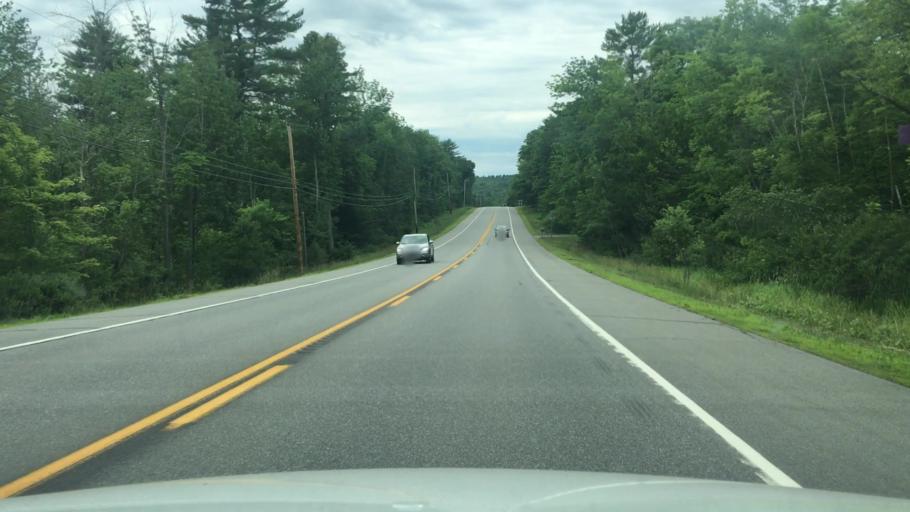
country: US
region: Maine
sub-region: Kennebec County
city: Windsor
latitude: 44.3444
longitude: -69.6541
